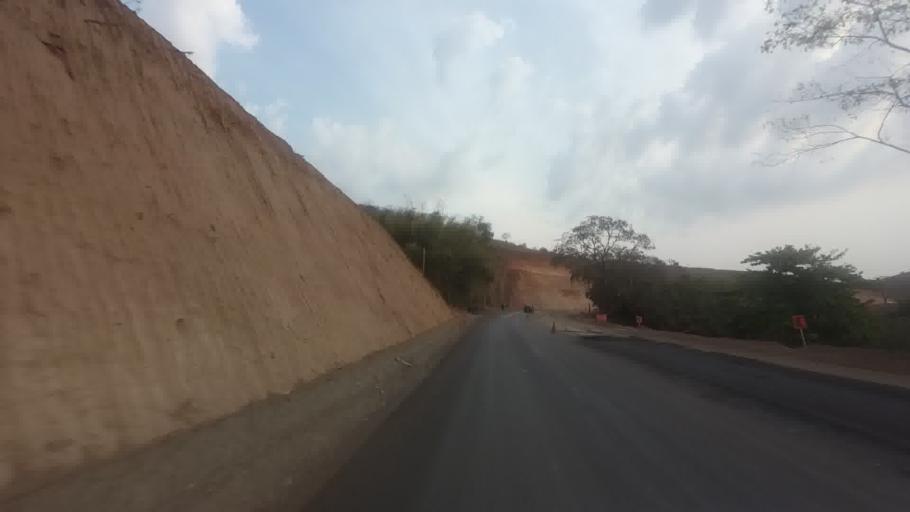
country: BR
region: Rio de Janeiro
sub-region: Santo Antonio De Padua
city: Santo Antonio de Padua
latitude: -21.5082
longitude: -42.0874
